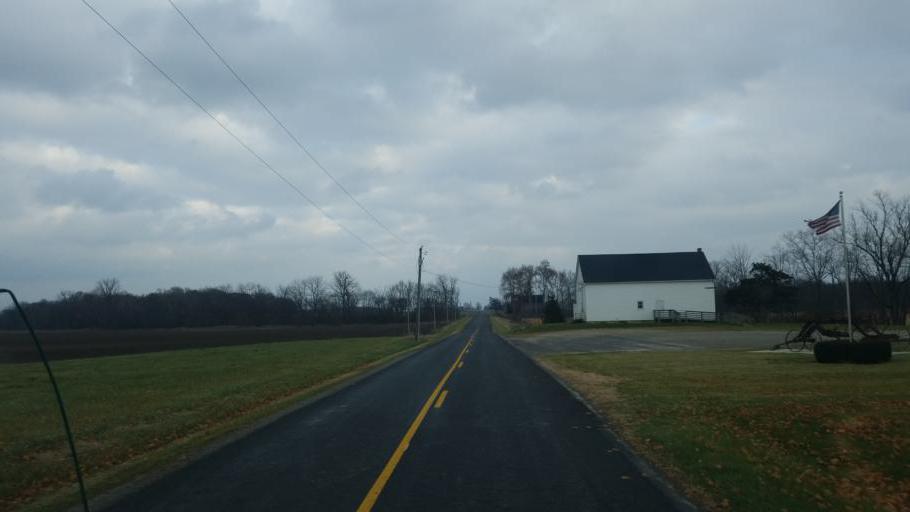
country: US
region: Ohio
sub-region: Mercer County
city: Fort Recovery
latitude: 40.5090
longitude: -84.7475
